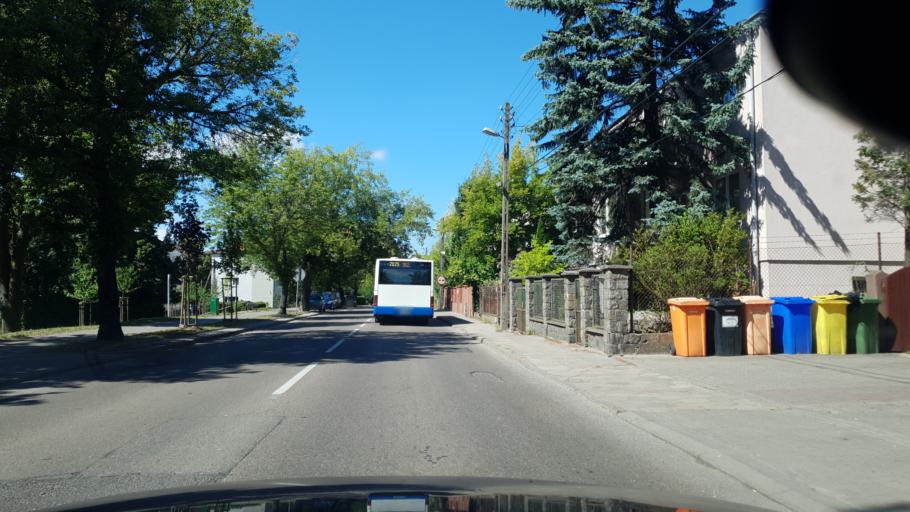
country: PL
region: Pomeranian Voivodeship
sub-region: Gdynia
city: Gdynia
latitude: 54.5006
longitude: 18.5414
